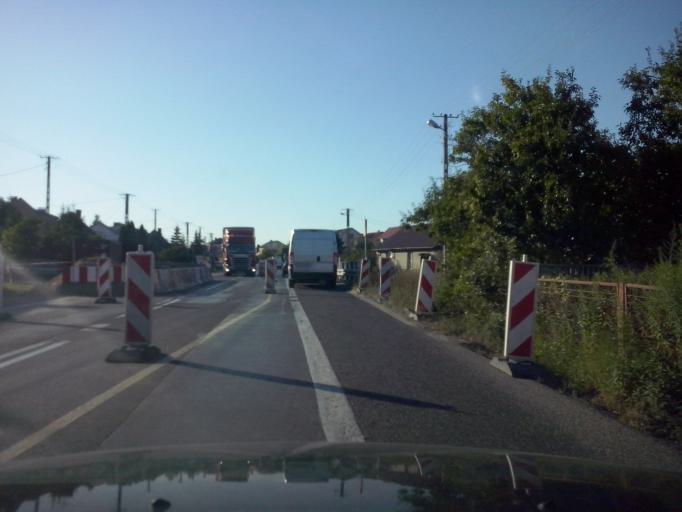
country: PL
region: Swietokrzyskie
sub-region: Powiat kielecki
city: Morawica
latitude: 50.7333
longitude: 20.6406
